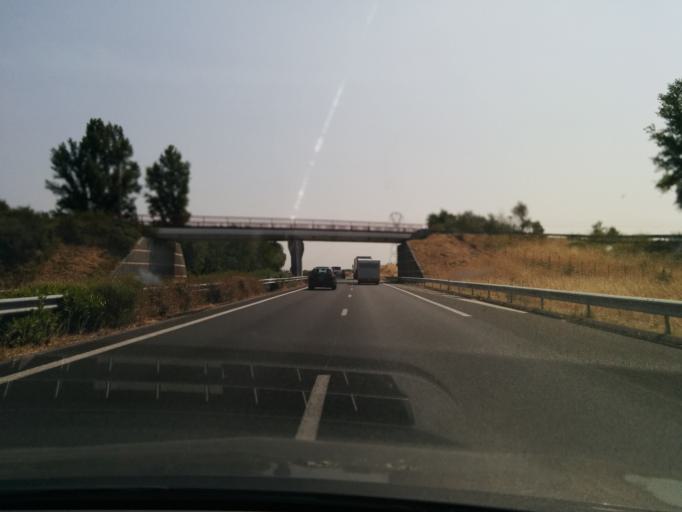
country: FR
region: Midi-Pyrenees
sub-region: Departement du Tarn
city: Brens
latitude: 43.8857
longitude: 1.9408
